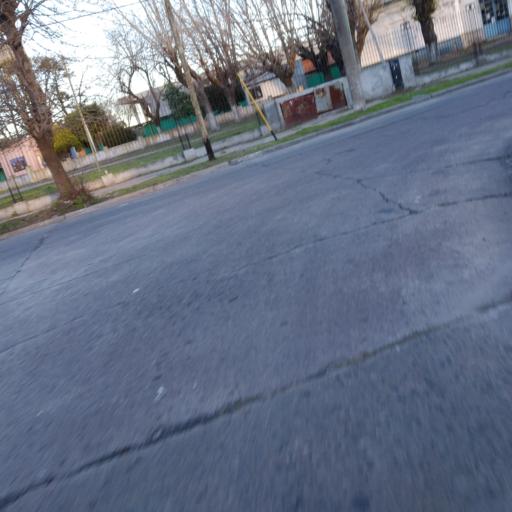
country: AR
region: Buenos Aires
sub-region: Partido de La Plata
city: La Plata
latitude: -34.9471
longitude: -57.9499
